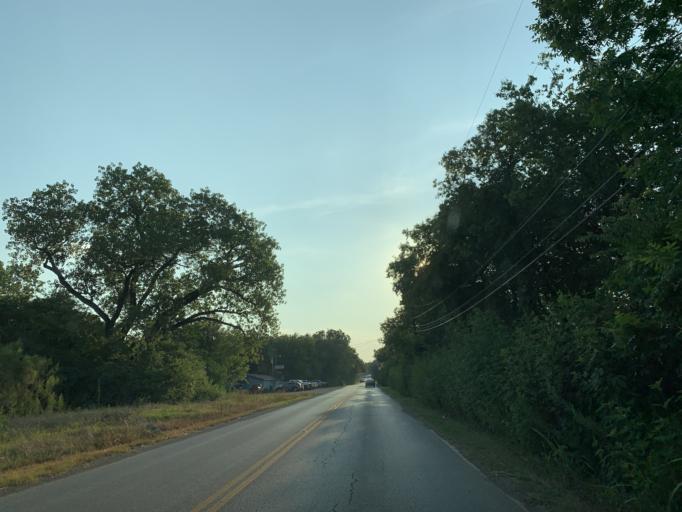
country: US
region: Texas
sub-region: Tarrant County
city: Hurst
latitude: 32.7798
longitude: -97.1808
